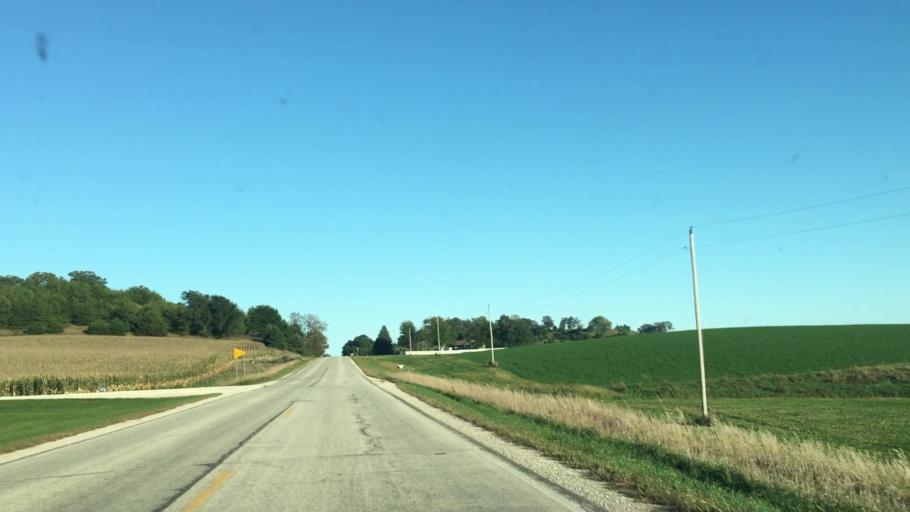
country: US
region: Minnesota
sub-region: Fillmore County
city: Chatfield
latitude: 43.8424
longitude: -92.0899
